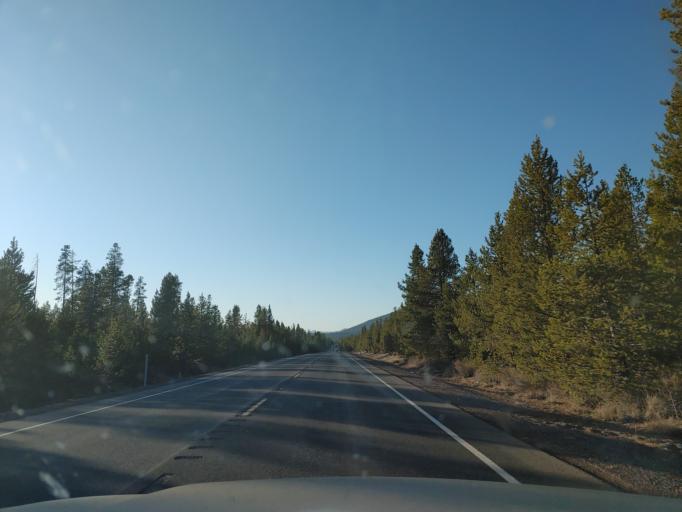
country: US
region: Oregon
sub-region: Deschutes County
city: La Pine
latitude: 43.4006
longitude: -121.8212
